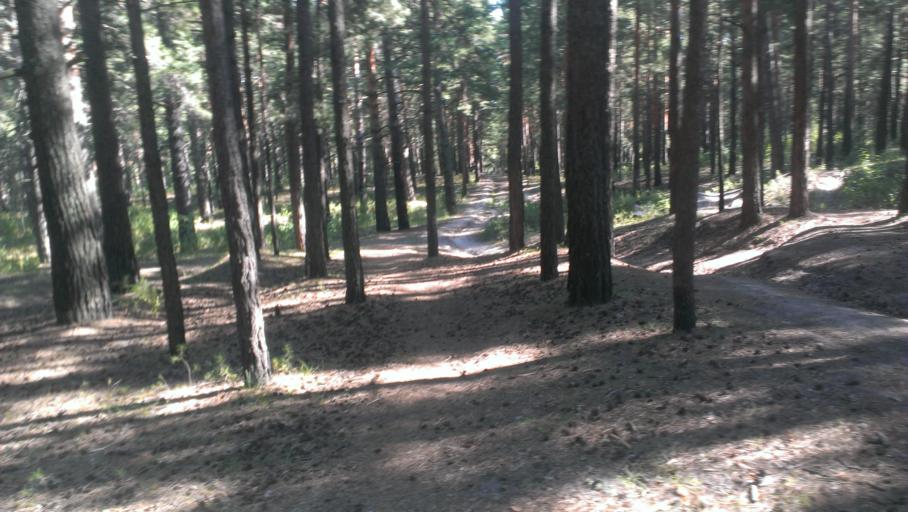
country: RU
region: Altai Krai
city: Novosilikatnyy
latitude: 53.3182
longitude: 83.6867
